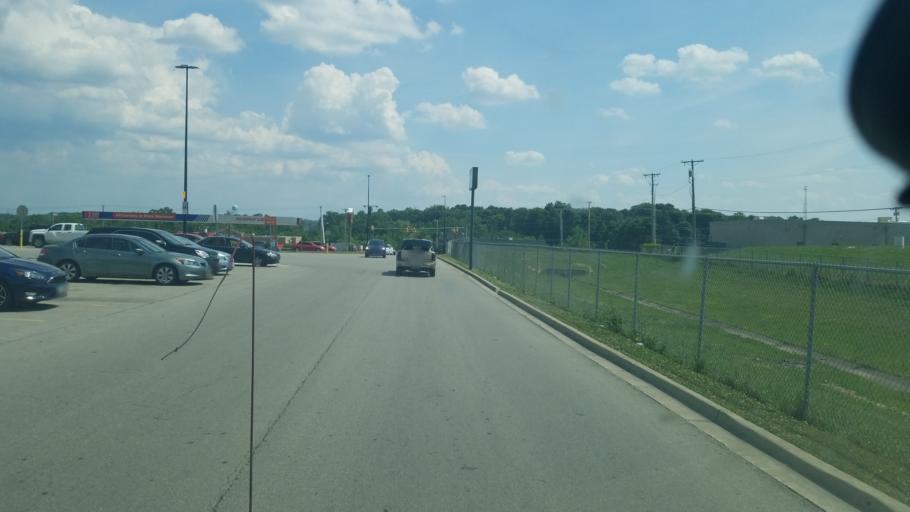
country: US
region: Ohio
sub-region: Highland County
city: Hillsboro
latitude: 39.2272
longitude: -83.6232
